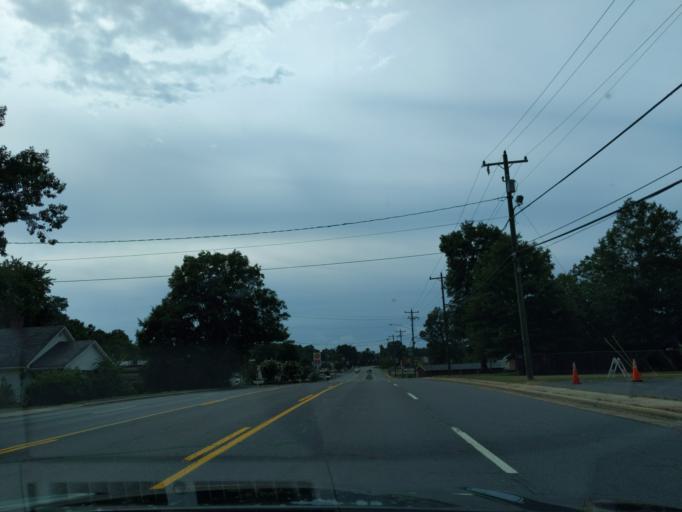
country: US
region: North Carolina
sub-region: Stanly County
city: Albemarle
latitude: 35.4703
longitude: -80.2647
